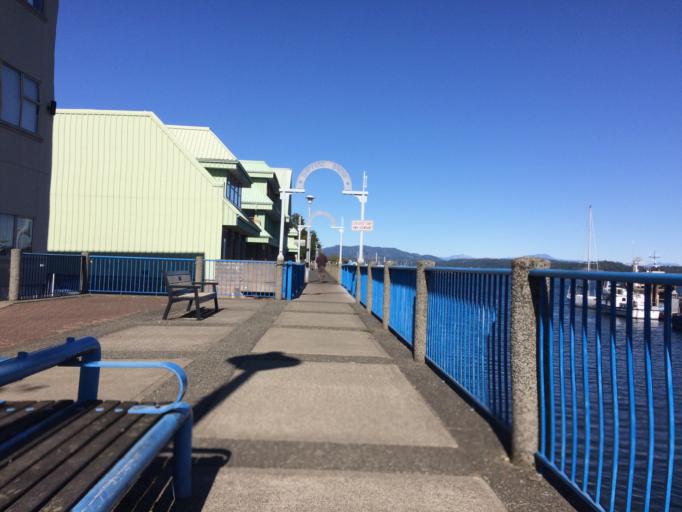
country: CA
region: British Columbia
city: Campbell River
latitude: 50.0230
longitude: -125.2393
